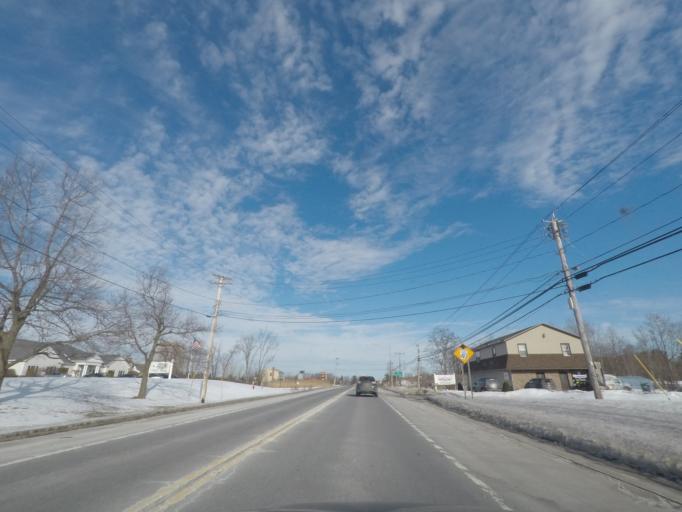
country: US
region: New York
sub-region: Schenectady County
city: Rotterdam
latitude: 42.7797
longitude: -74.0317
